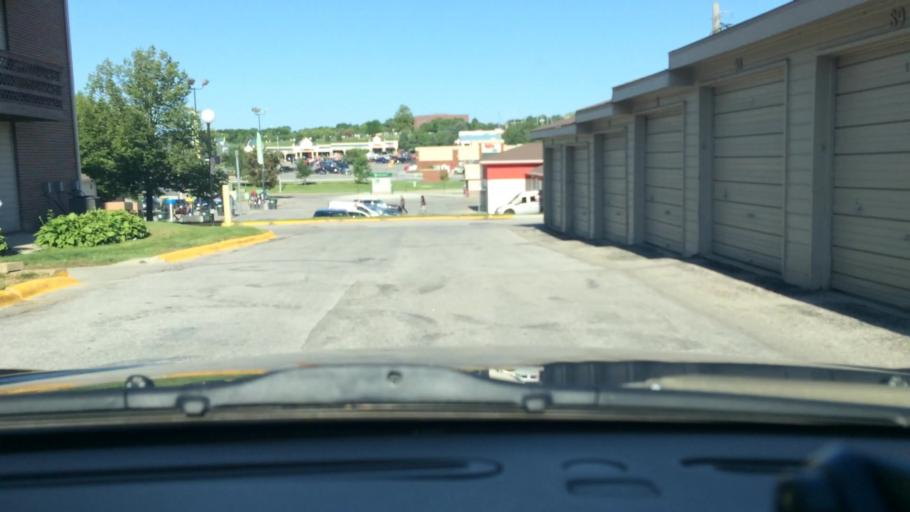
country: US
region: Nebraska
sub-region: Douglas County
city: Ralston
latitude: 41.2046
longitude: -96.0603
